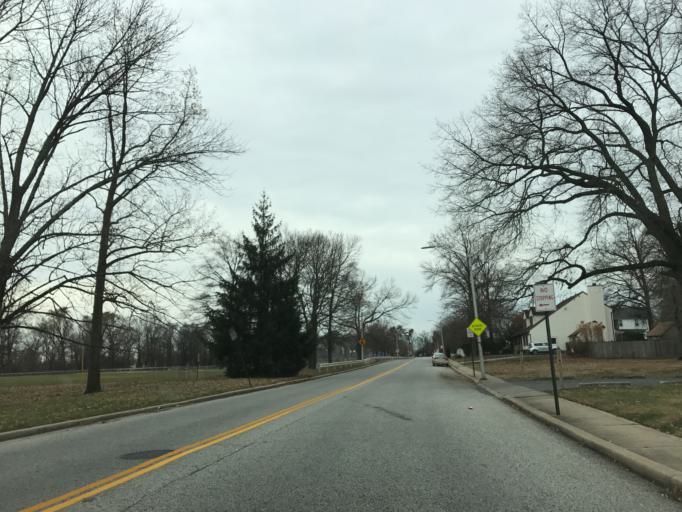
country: US
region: Maryland
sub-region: Baltimore County
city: Parkville
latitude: 39.3687
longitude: -76.5382
